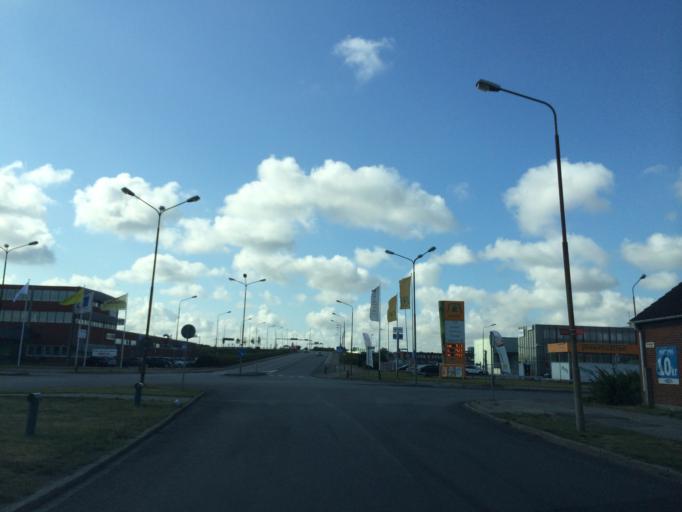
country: SE
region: Skane
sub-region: Burlovs Kommun
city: Arloev
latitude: 55.6199
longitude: 13.0384
